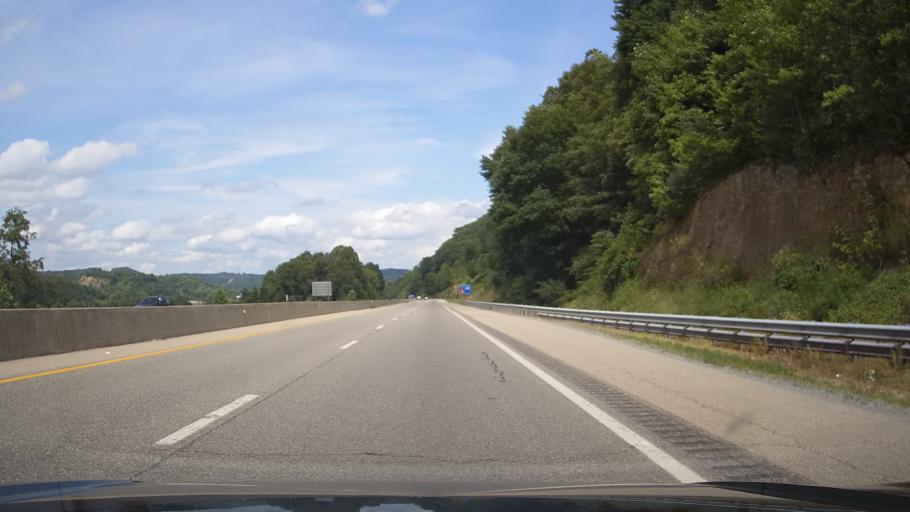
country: US
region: Virginia
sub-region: City of Norton
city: Norton
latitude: 36.9296
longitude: -82.6280
